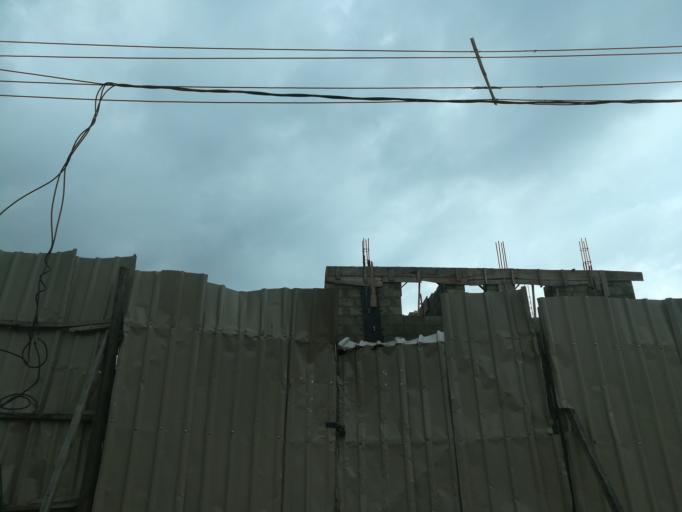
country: NG
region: Lagos
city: Oshodi
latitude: 6.5518
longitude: 3.3381
